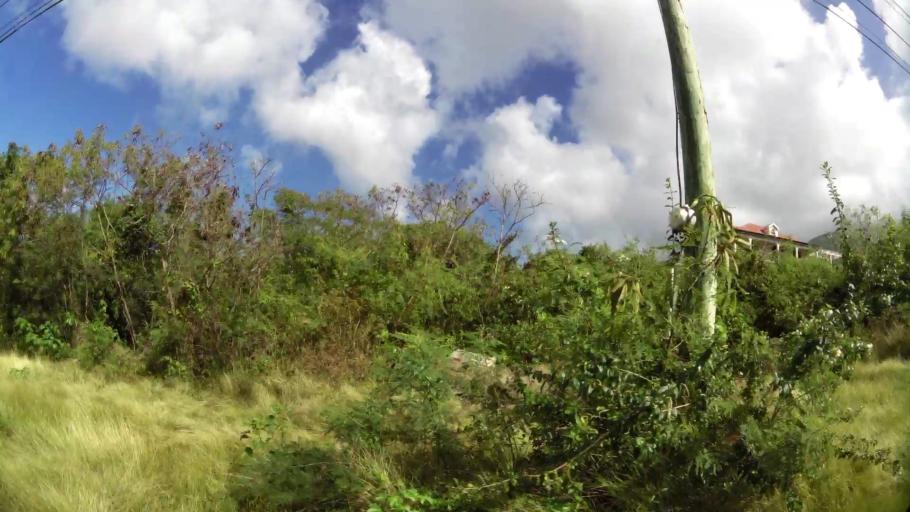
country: KN
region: Saint Paul Charlestown
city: Charlestown
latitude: 17.1338
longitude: -62.6125
